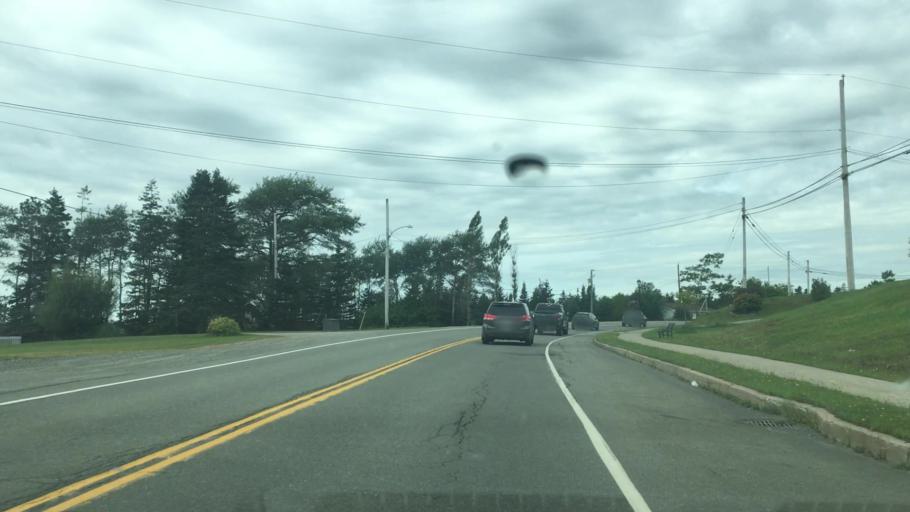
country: CA
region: Nova Scotia
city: Princeville
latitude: 45.6544
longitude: -60.8910
